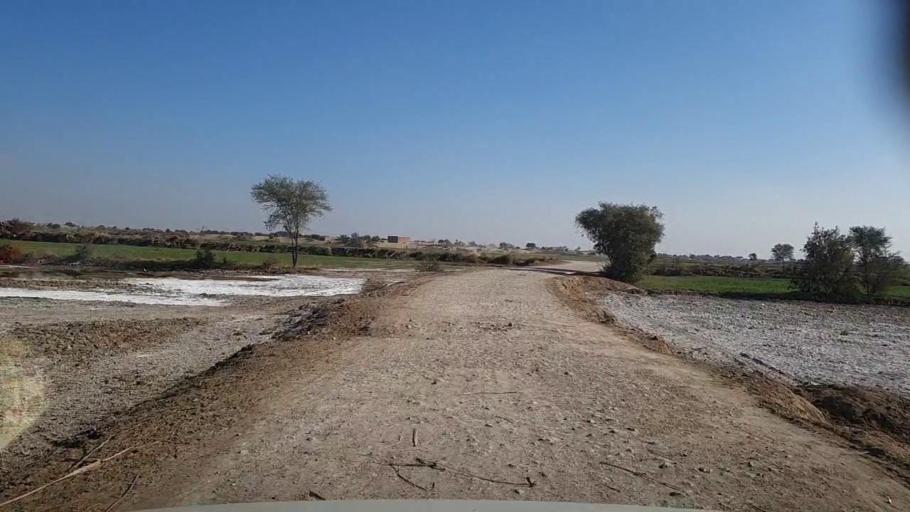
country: PK
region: Sindh
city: Khairpur
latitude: 27.9253
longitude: 69.7362
